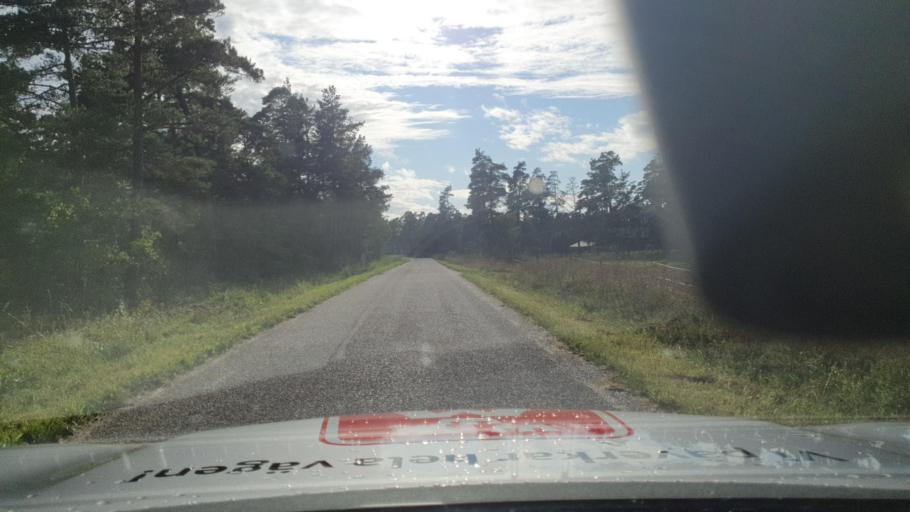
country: SE
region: Gotland
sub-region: Gotland
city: Slite
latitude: 57.5836
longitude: 18.6964
